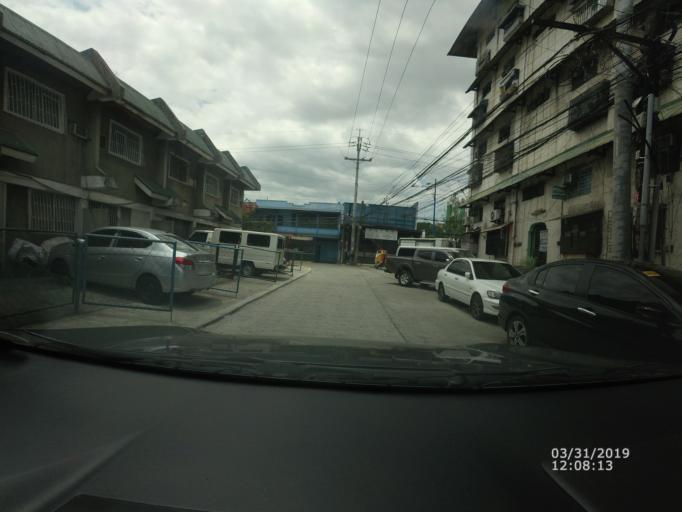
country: PH
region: Metro Manila
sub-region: Mandaluyong
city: Mandaluyong City
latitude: 14.5786
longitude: 121.0295
